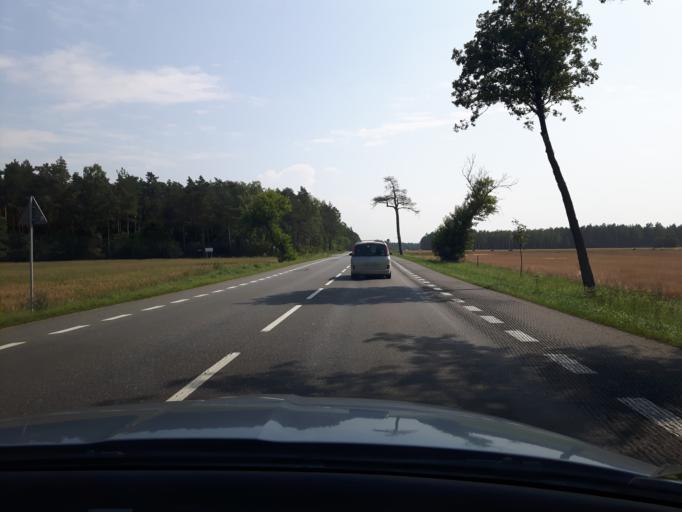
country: PL
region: Masovian Voivodeship
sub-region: Powiat mlawski
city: Strzegowo
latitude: 52.9272
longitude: 20.2860
